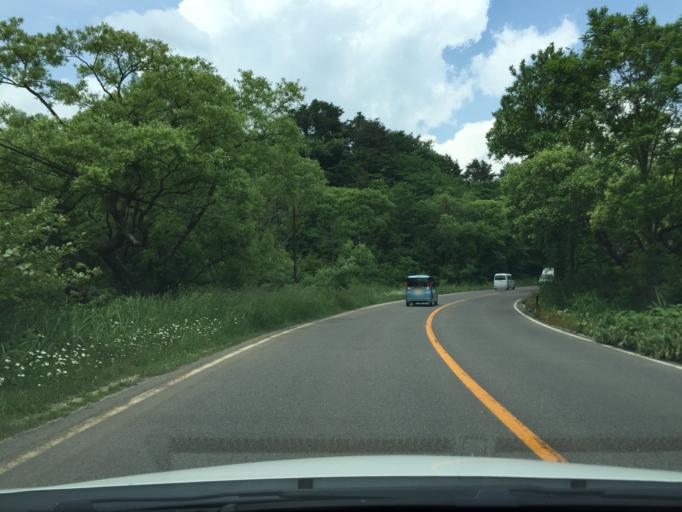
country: JP
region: Fukushima
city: Inawashiro
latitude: 37.6453
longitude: 140.0992
